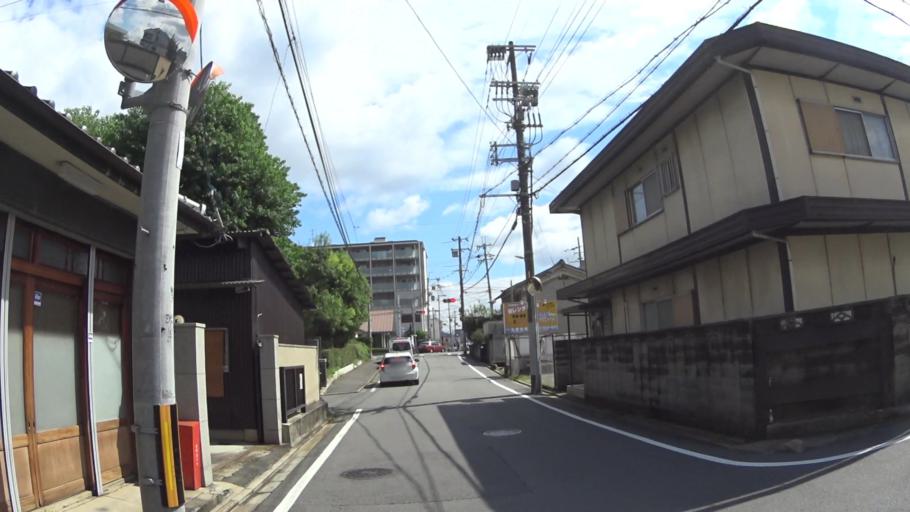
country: JP
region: Kyoto
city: Muko
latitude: 34.9889
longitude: 135.7236
